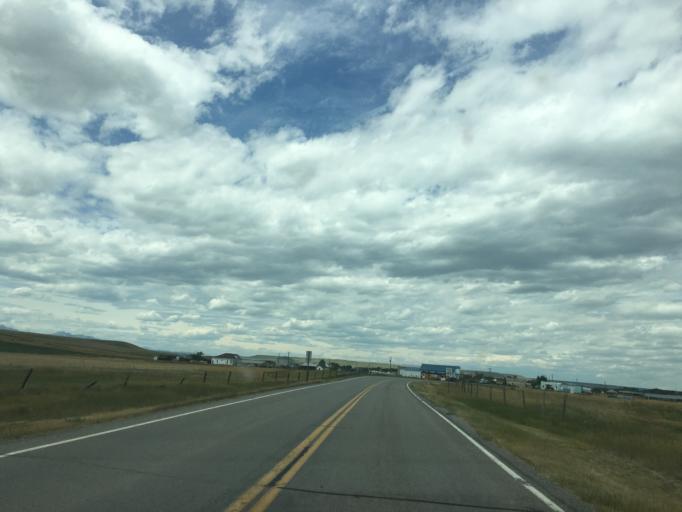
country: US
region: Montana
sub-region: Teton County
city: Choteau
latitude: 47.9737
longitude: -112.3088
